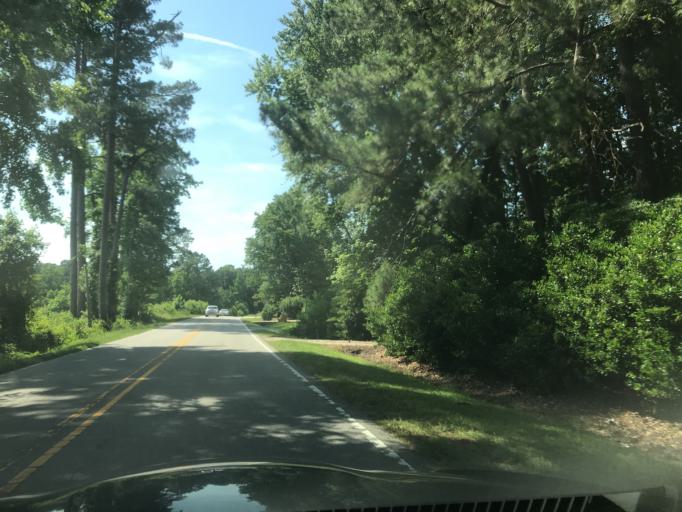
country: US
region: North Carolina
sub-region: Wake County
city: Wendell
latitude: 35.7693
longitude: -78.3565
